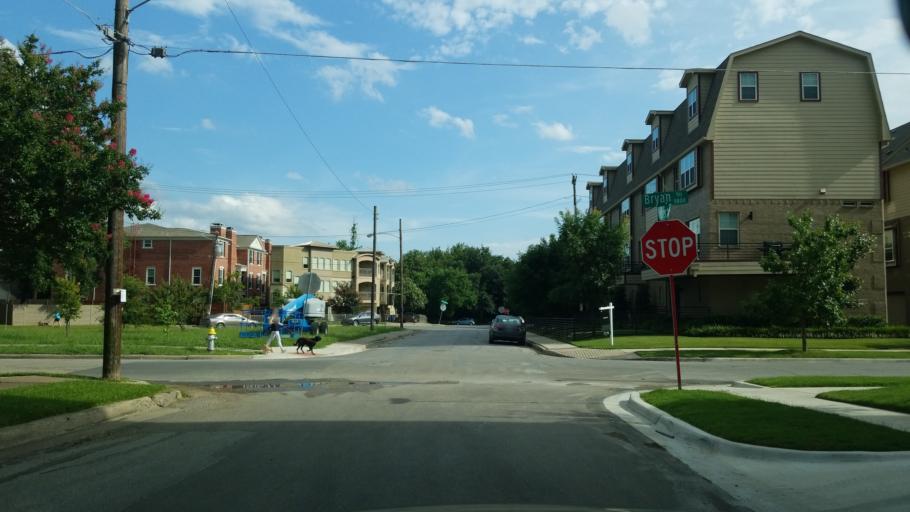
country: US
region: Texas
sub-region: Dallas County
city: Highland Park
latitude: 32.8081
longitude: -96.7669
